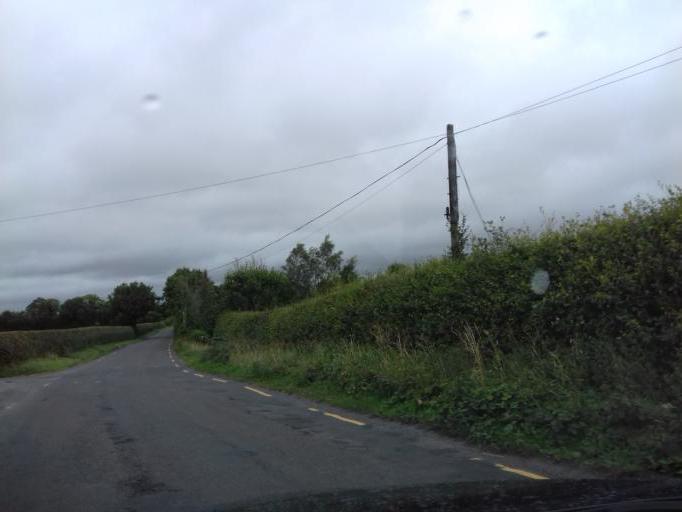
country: IE
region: Leinster
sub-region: Kilkenny
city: Graiguenamanagh
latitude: 52.6143
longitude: -7.0338
